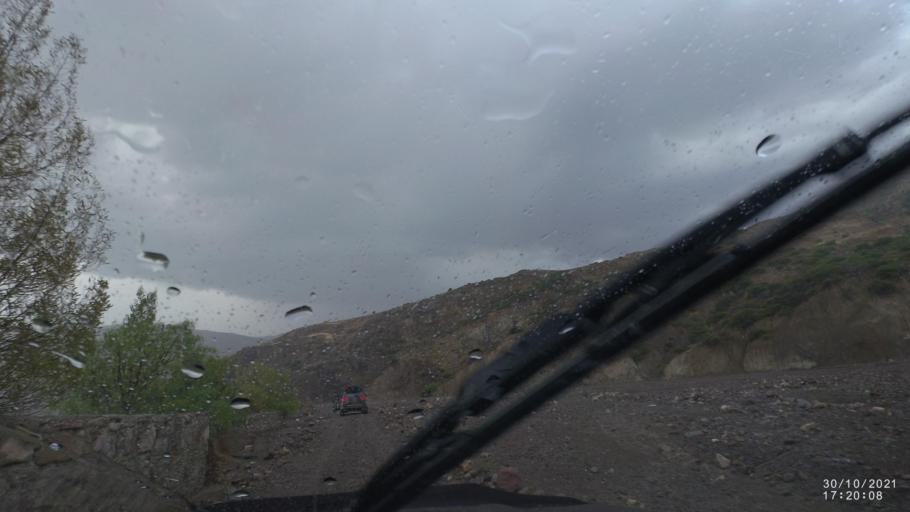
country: BO
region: Cochabamba
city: Colchani
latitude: -17.5320
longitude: -66.6198
